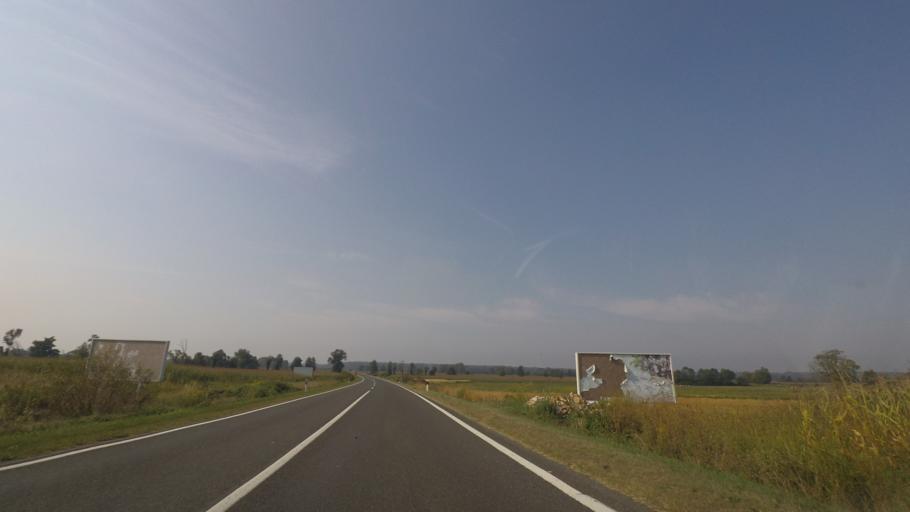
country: HR
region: Sisacko-Moslavacka
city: Novska
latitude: 45.3500
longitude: 16.9634
